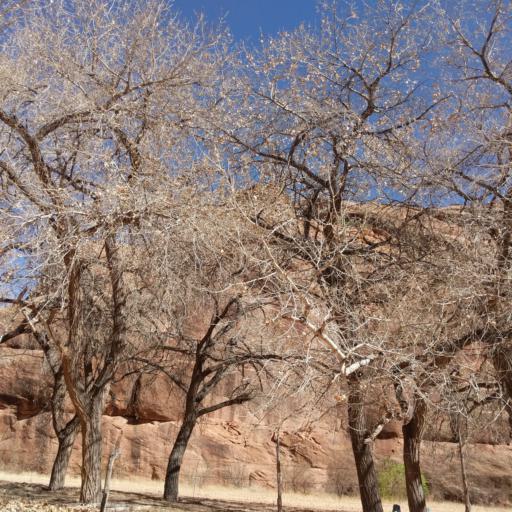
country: US
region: Arizona
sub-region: Apache County
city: Chinle
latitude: 36.1588
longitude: -109.4655
